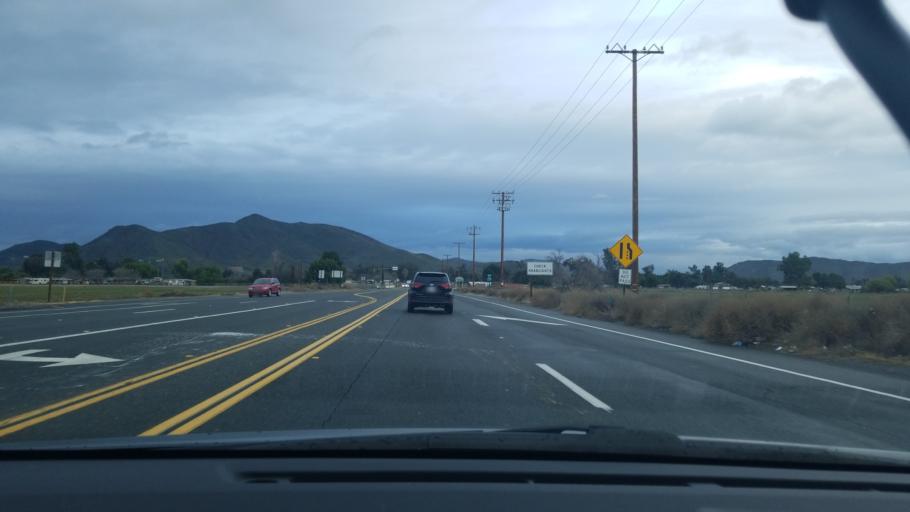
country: US
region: California
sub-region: Riverside County
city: Winchester
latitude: 33.6967
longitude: -117.0848
